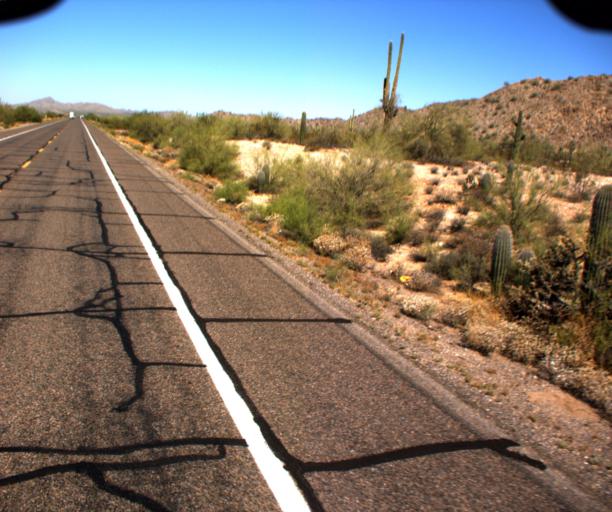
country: US
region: Arizona
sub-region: Pinal County
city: Sacaton
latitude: 33.0040
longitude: -111.7292
